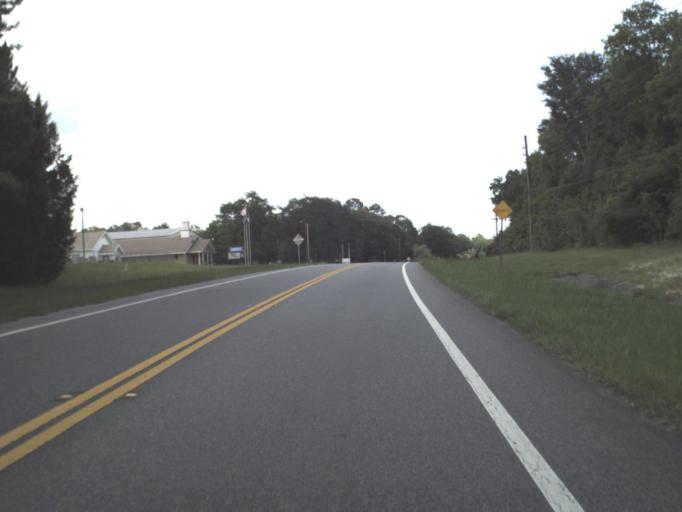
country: US
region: Florida
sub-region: Clay County
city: Asbury Lake
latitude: 29.9818
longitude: -81.8451
